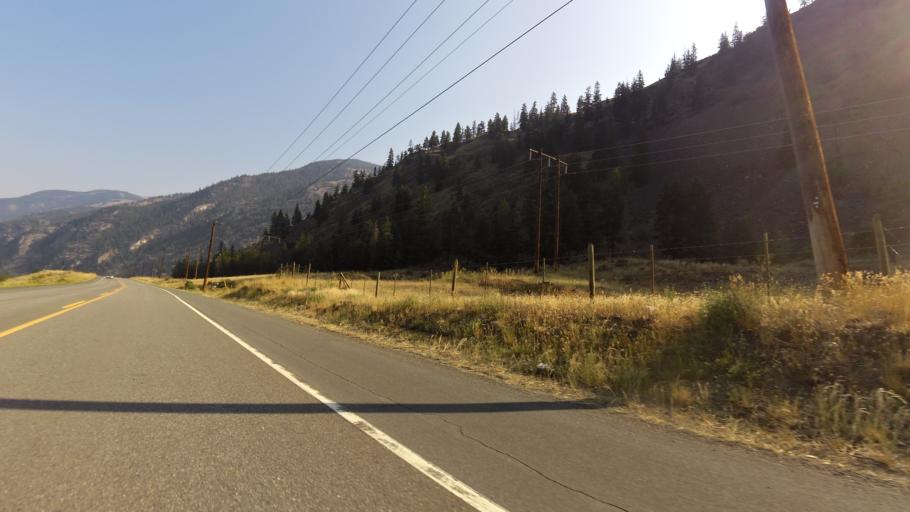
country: CA
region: British Columbia
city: Summerland
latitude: 49.2988
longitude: -120.0273
